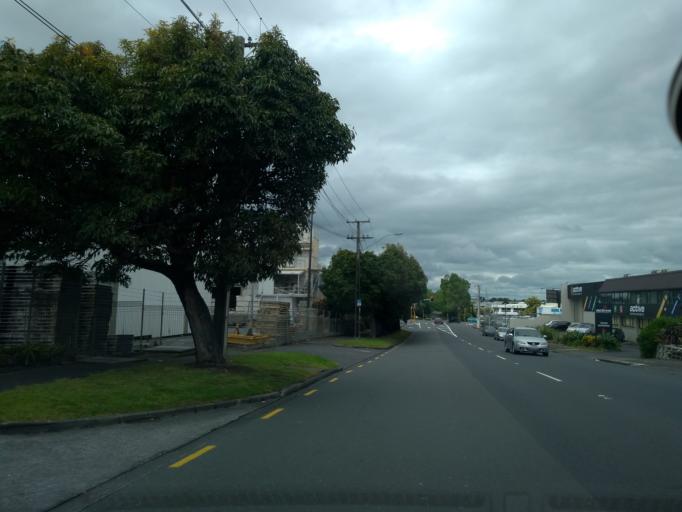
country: NZ
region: Auckland
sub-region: Auckland
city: Tamaki
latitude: -36.9182
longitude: 174.8189
